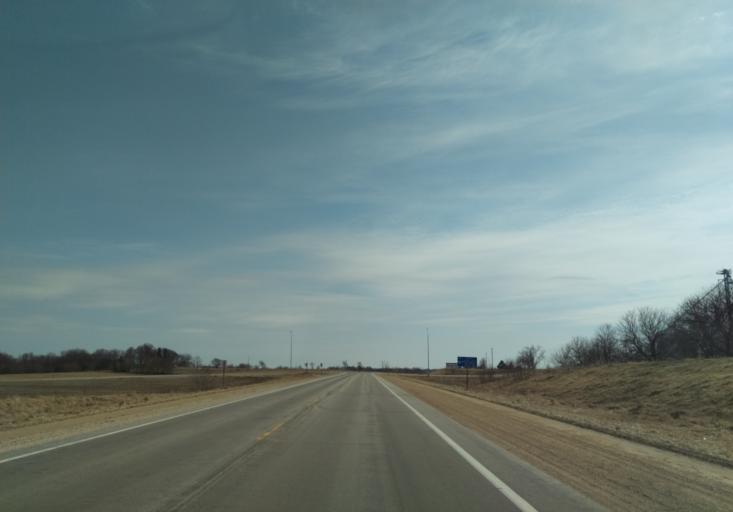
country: US
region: Iowa
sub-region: Winneshiek County
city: Decorah
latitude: 43.3693
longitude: -91.8083
